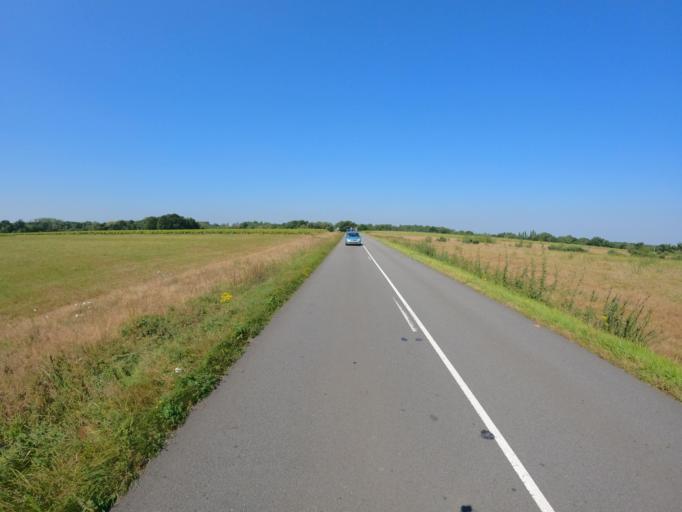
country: FR
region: Pays de la Loire
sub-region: Departement de la Loire-Atlantique
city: Pont-Saint-Martin
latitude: 47.1195
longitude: -1.5639
